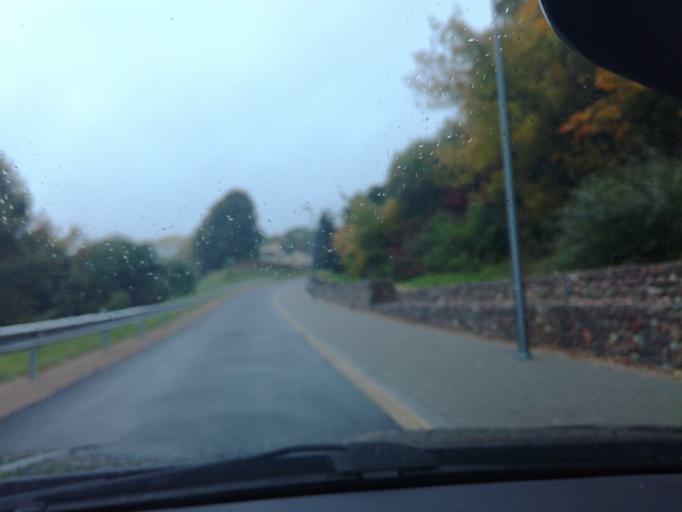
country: LT
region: Alytaus apskritis
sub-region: Alytus
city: Alytus
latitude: 54.3980
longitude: 24.0729
